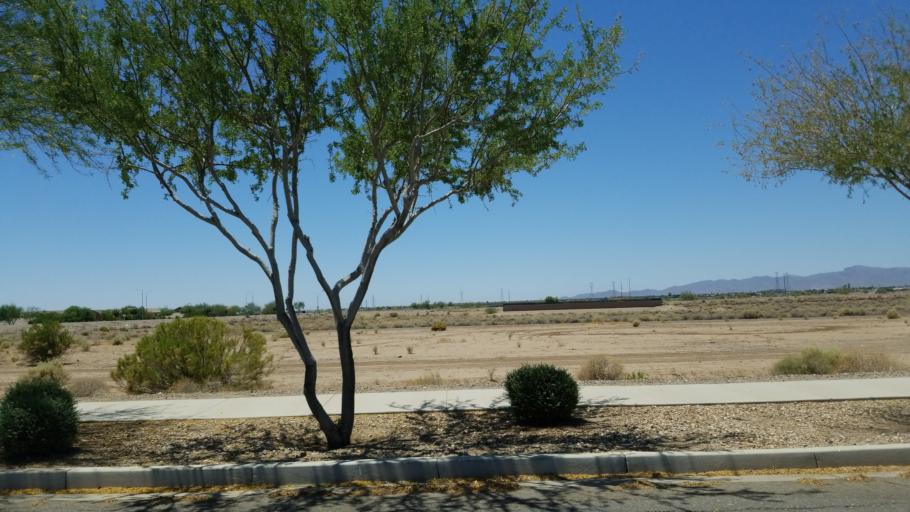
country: US
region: Arizona
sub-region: Maricopa County
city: Litchfield Park
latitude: 33.5098
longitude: -112.2990
